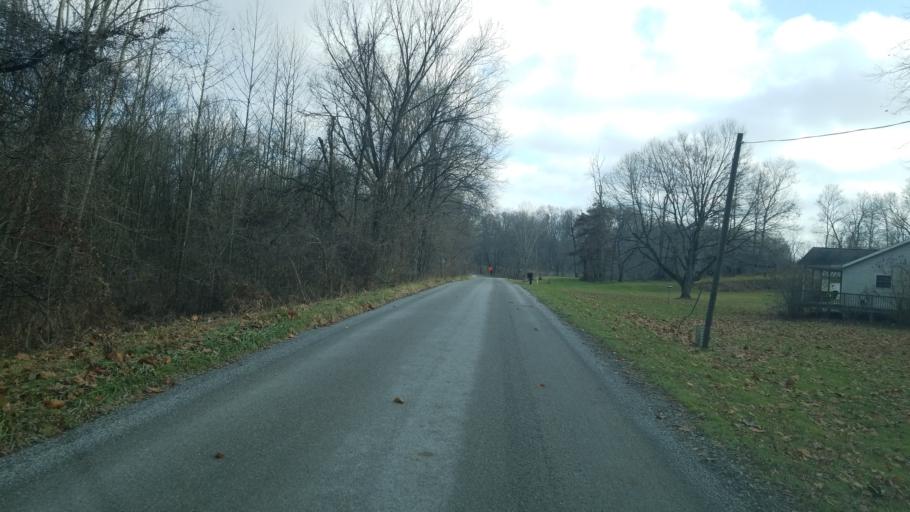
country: US
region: Ohio
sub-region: Richland County
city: Lincoln Heights
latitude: 40.8188
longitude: -82.4081
